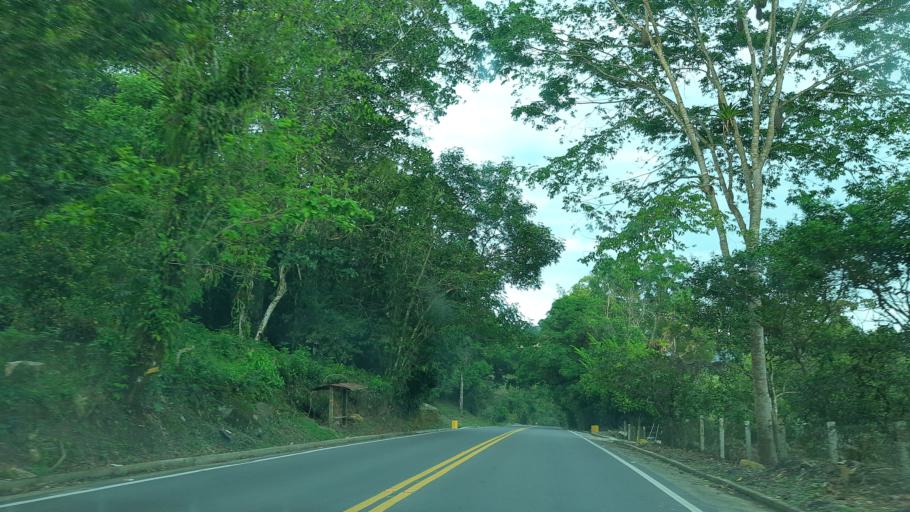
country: CO
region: Boyaca
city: San Luis de Gaceno
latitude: 4.8314
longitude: -73.1412
